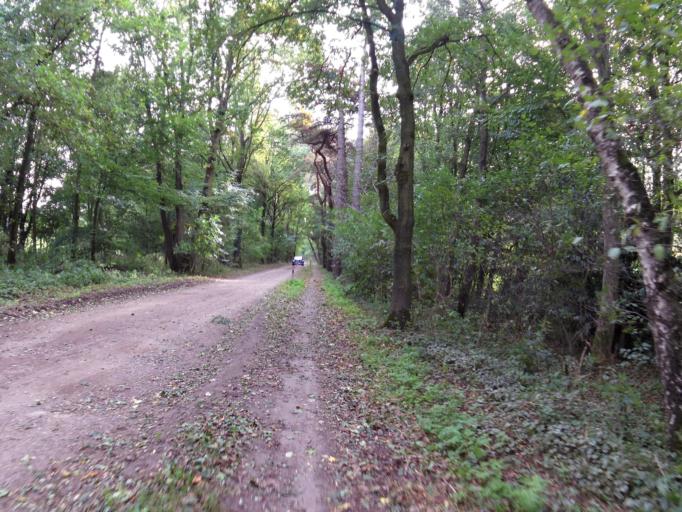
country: NL
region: North Brabant
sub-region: Gemeente Vught
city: Vught
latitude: 51.6297
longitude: 5.2685
